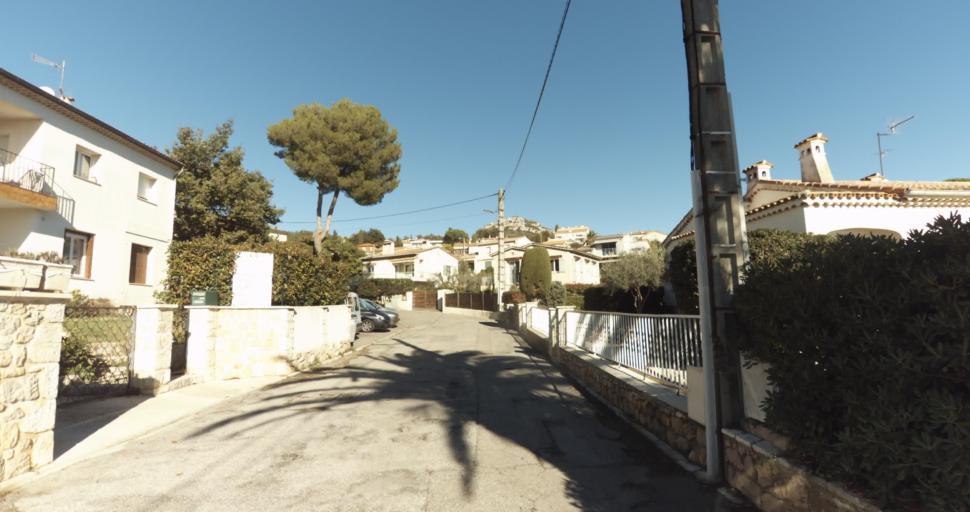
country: FR
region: Provence-Alpes-Cote d'Azur
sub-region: Departement des Alpes-Maritimes
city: Vence
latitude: 43.7182
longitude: 7.1049
